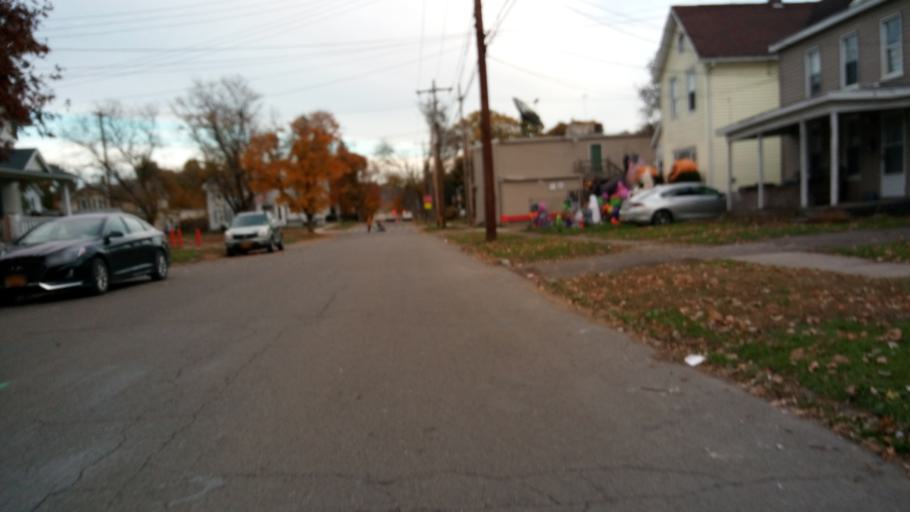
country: US
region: New York
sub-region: Chemung County
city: Elmira
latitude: 42.0755
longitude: -76.8027
